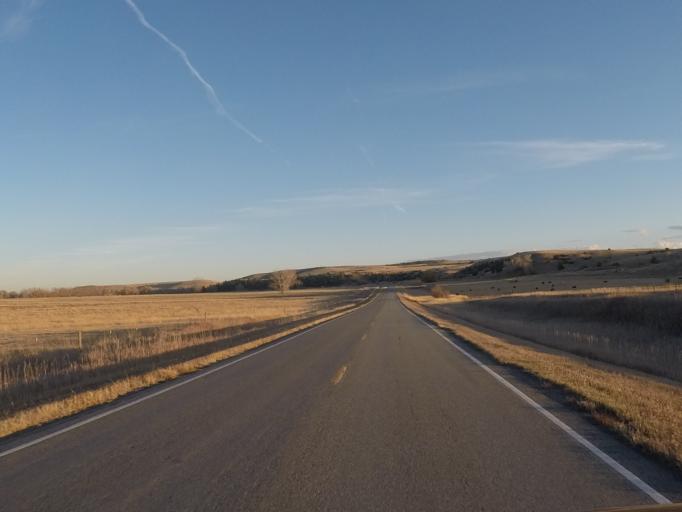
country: US
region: Montana
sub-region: Sweet Grass County
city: Big Timber
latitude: 45.7921
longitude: -109.8548
